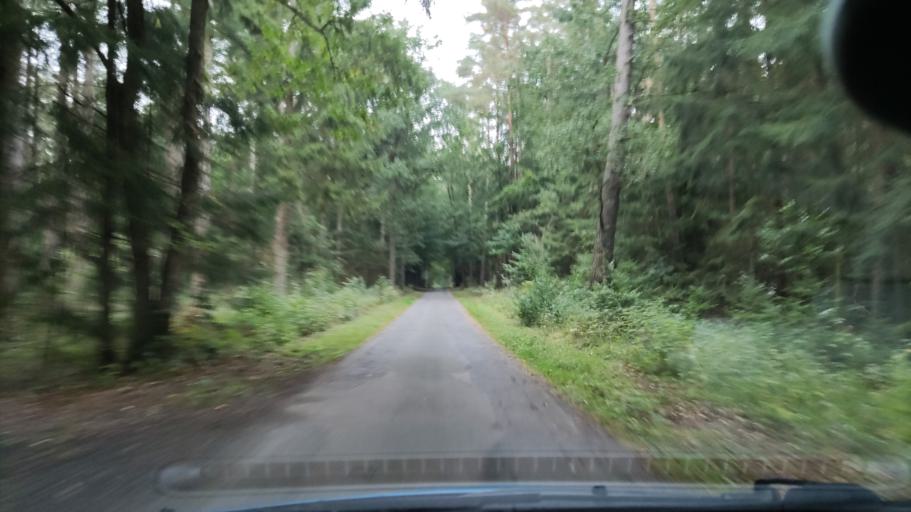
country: DE
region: Lower Saxony
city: Karwitz
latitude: 53.0879
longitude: 10.9764
